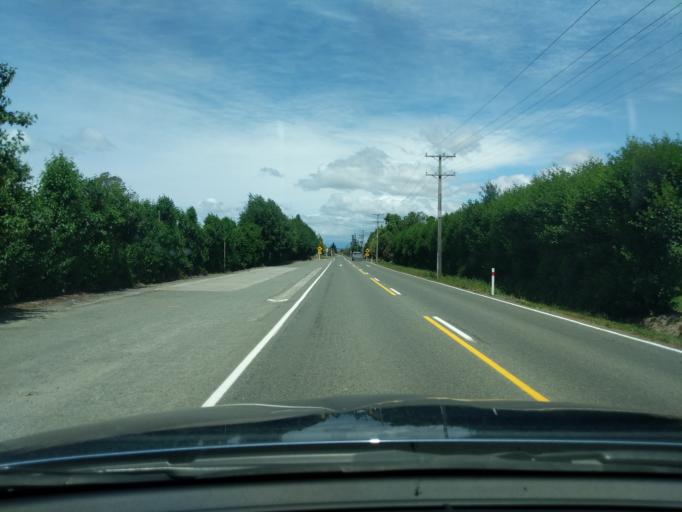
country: NZ
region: Tasman
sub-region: Tasman District
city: Motueka
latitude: -41.0885
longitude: 172.9968
